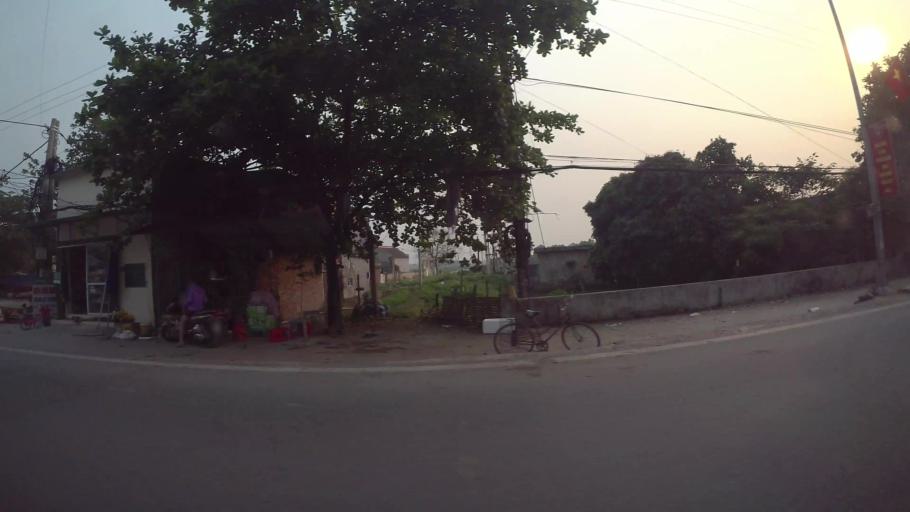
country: VN
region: Ha Noi
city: Thuong Tin
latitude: 20.8690
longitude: 105.8294
